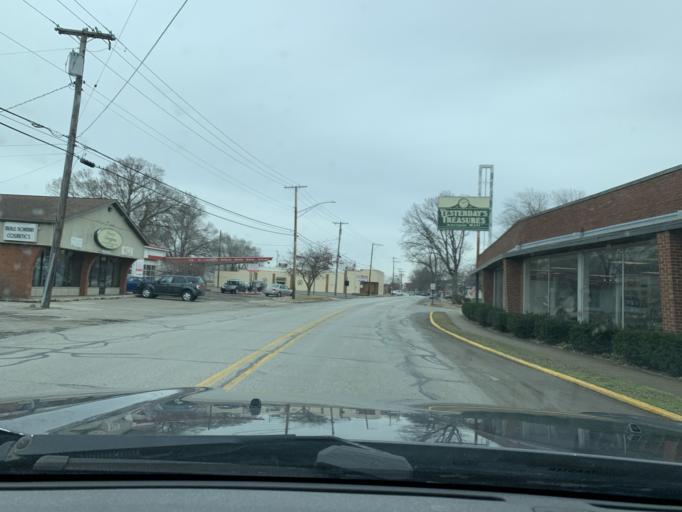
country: US
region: Indiana
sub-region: Porter County
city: Chesterton
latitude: 41.6116
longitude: -87.0612
